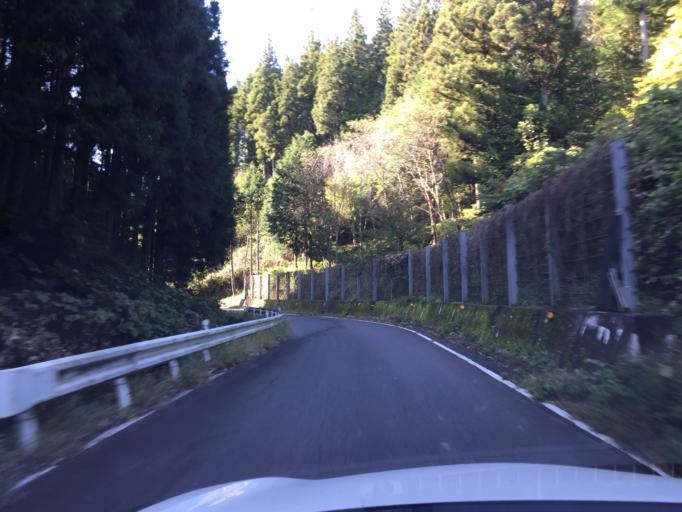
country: JP
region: Fukushima
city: Ishikawa
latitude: 37.1284
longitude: 140.5542
